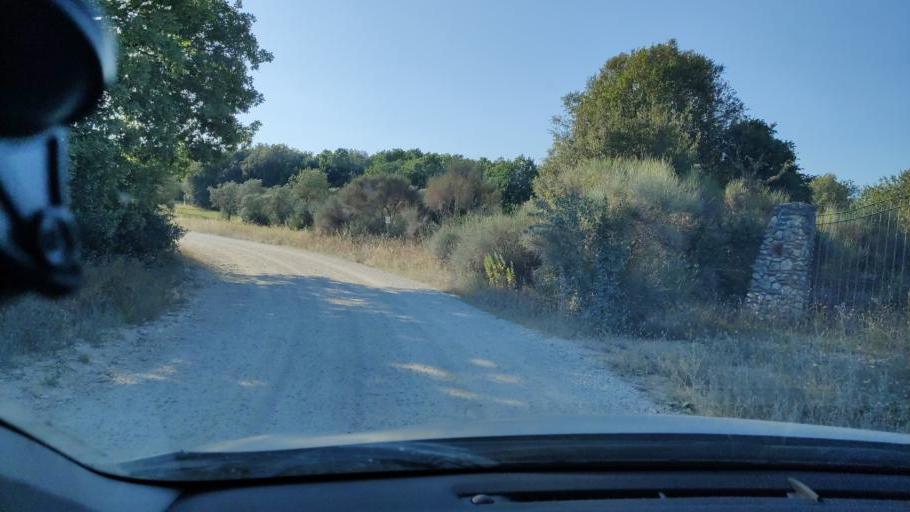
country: IT
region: Umbria
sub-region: Provincia di Terni
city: Amelia
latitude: 42.5383
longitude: 12.3792
